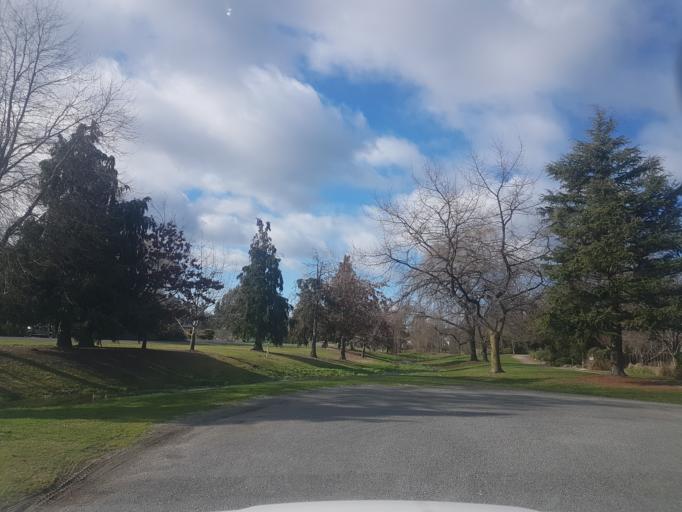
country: NZ
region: Canterbury
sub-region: Timaru District
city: Pleasant Point
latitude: -44.2590
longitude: 171.1248
